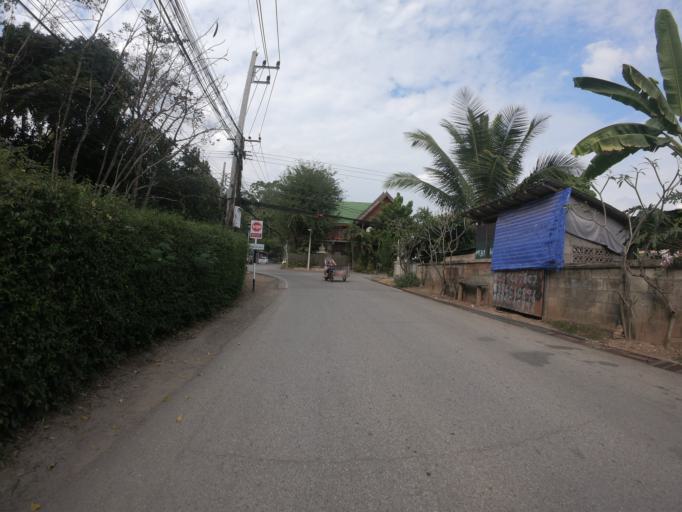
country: TH
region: Chiang Mai
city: Chiang Mai
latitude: 18.7692
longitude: 98.9453
